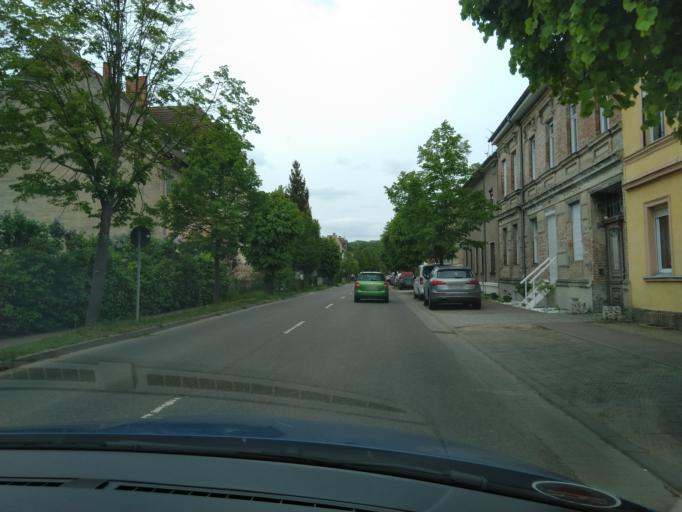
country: DE
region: Brandenburg
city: Oderberg
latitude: 52.8615
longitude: 14.0428
